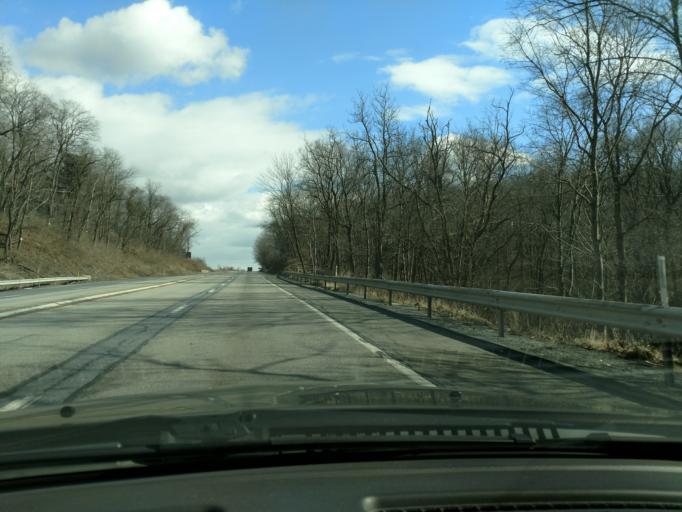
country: US
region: Pennsylvania
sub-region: Berks County
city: West Hamburg
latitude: 40.5719
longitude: -76.0165
